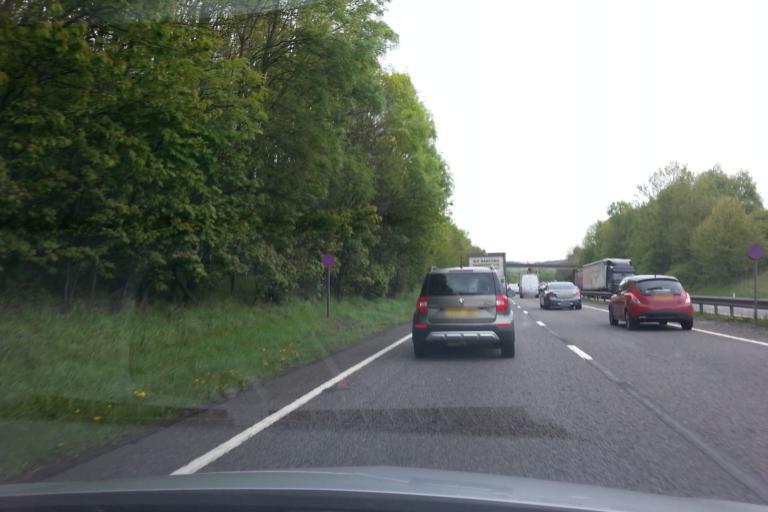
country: GB
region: England
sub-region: Derbyshire
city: Melbourne
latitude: 52.7913
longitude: -1.4044
